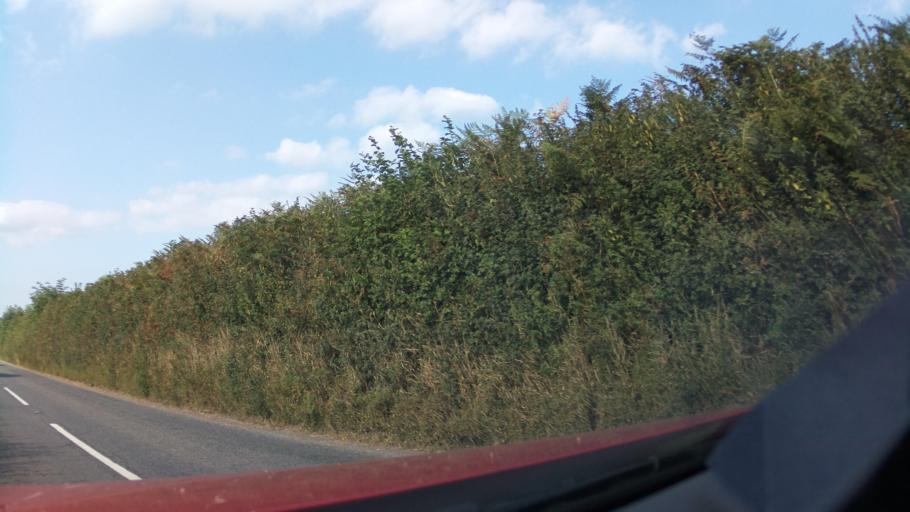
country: GB
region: England
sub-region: Devon
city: Tiverton
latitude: 50.8239
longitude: -3.4967
